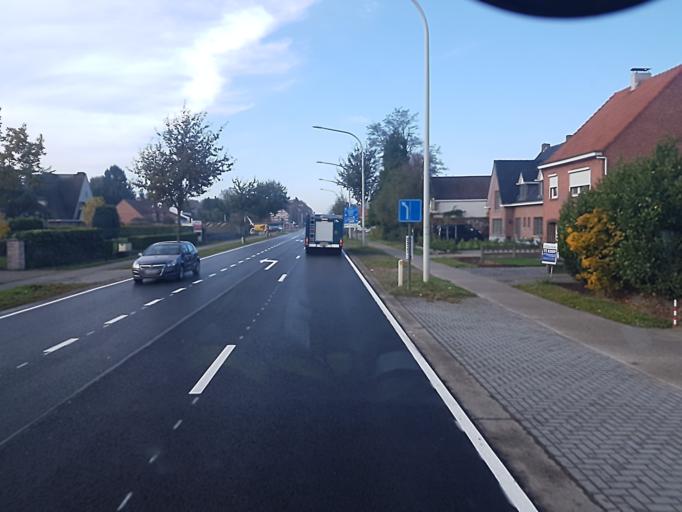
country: BE
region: Flanders
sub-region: Provincie Antwerpen
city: Beerse
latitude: 51.3109
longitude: 4.8600
